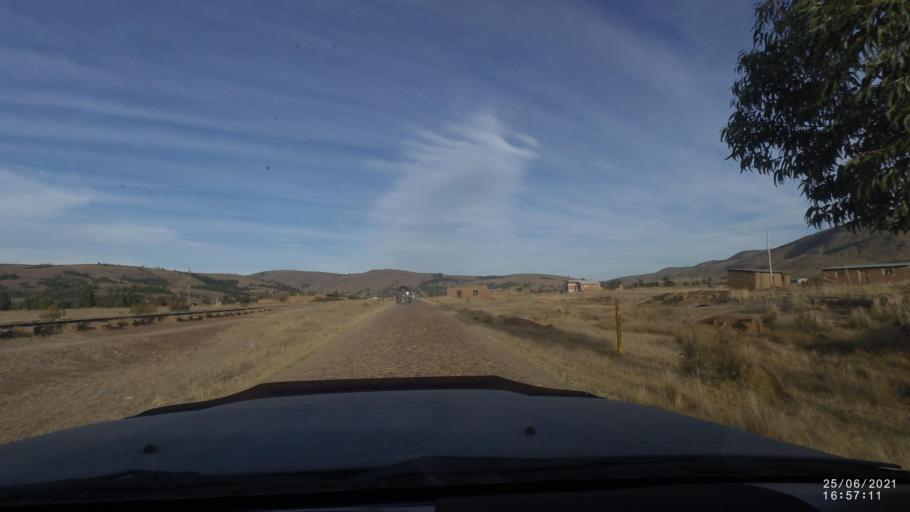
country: BO
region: Cochabamba
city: Arani
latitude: -17.8280
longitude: -65.7632
